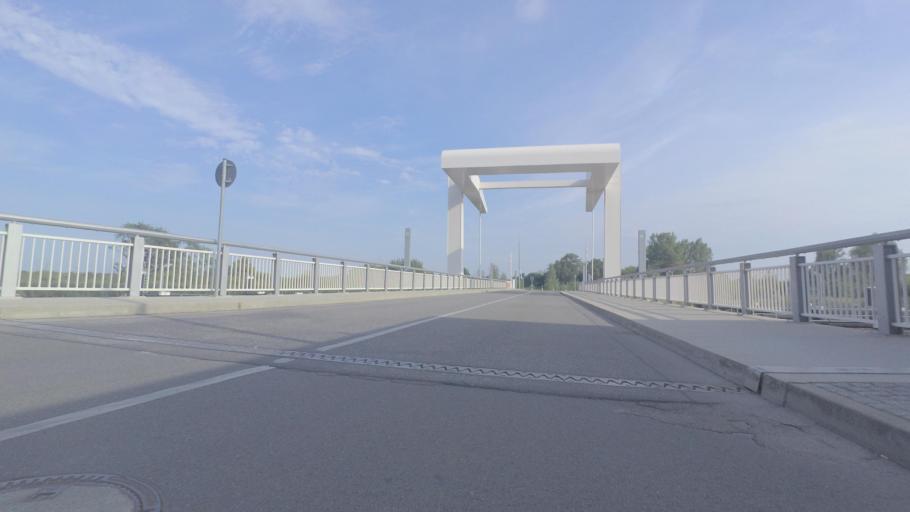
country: DE
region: Mecklenburg-Vorpommern
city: Demmin
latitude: 53.9689
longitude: 13.1317
